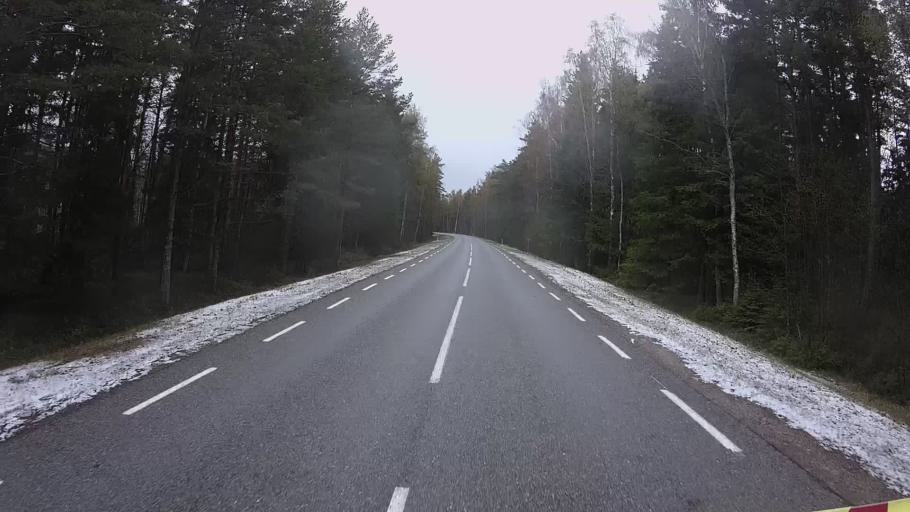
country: EE
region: Hiiumaa
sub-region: Kaerdla linn
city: Kardla
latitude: 59.0358
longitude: 22.6811
